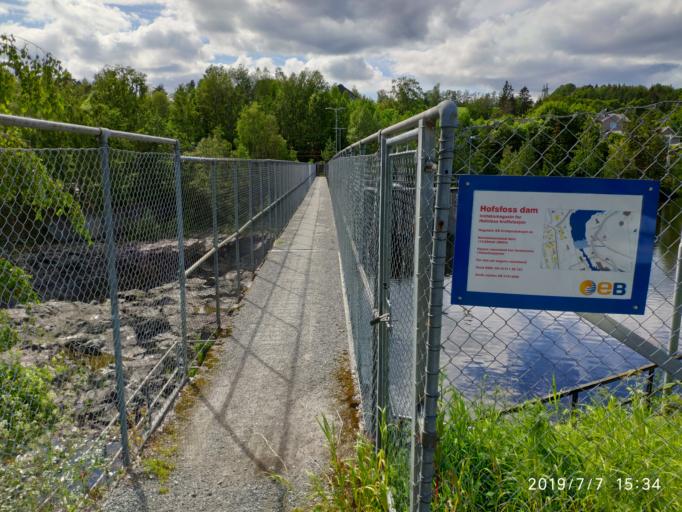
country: NO
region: Buskerud
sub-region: Ringerike
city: Honefoss
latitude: 60.1871
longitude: 10.2378
